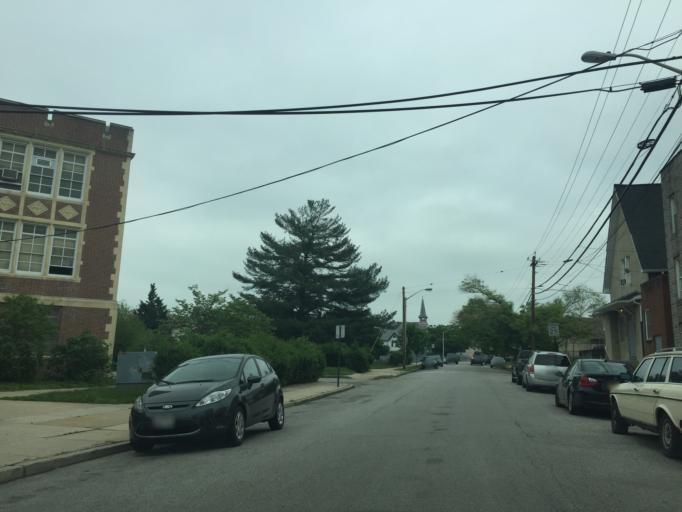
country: US
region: Maryland
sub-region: City of Baltimore
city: Baltimore
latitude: 39.3302
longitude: -76.6382
